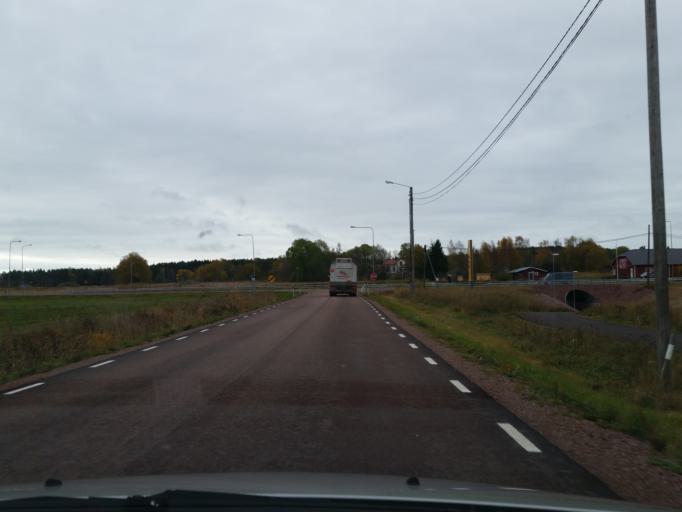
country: AX
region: Alands landsbygd
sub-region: Lemland
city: Lemland
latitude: 60.0700
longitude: 20.0858
